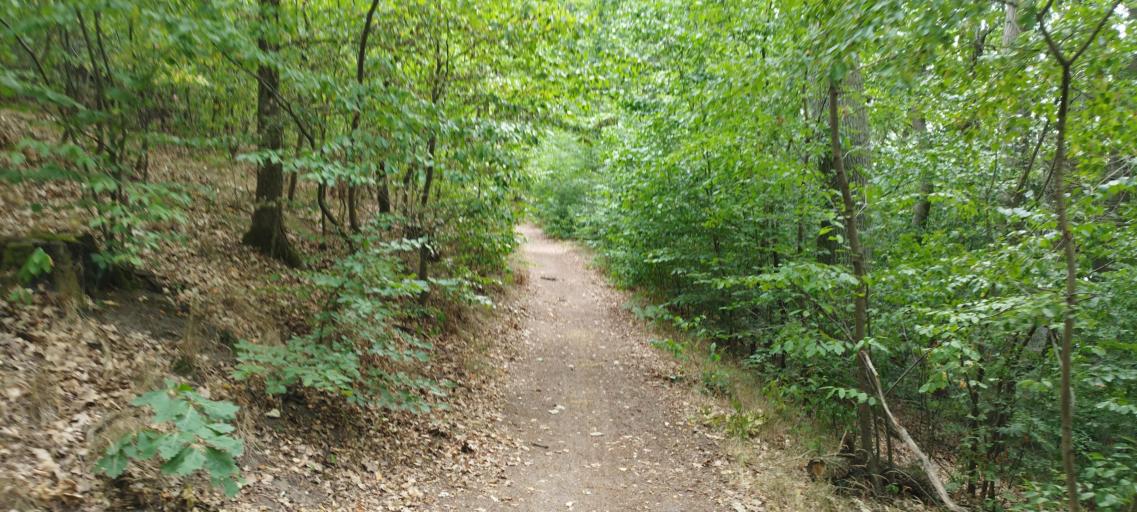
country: DE
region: Brandenburg
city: Strausberg
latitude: 52.5918
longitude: 13.8394
